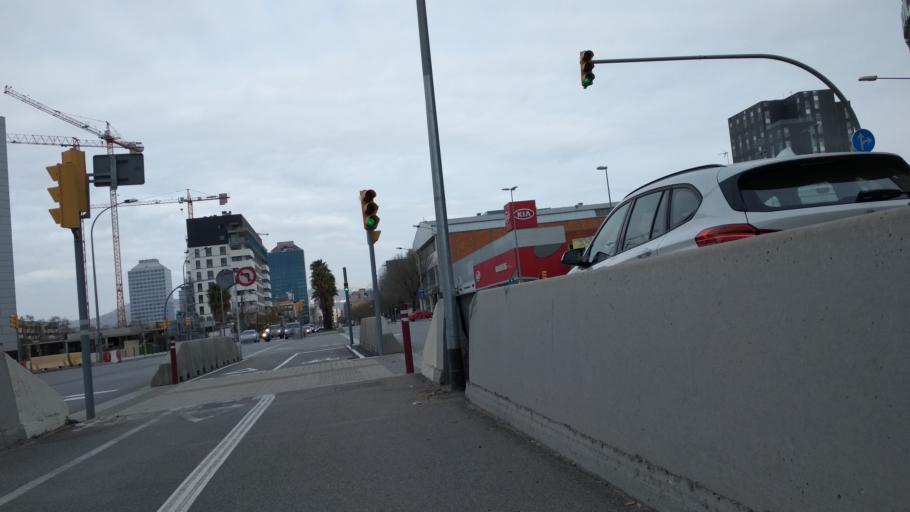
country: ES
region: Catalonia
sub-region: Provincia de Barcelona
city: Sants-Montjuic
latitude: 41.3506
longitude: 2.1459
